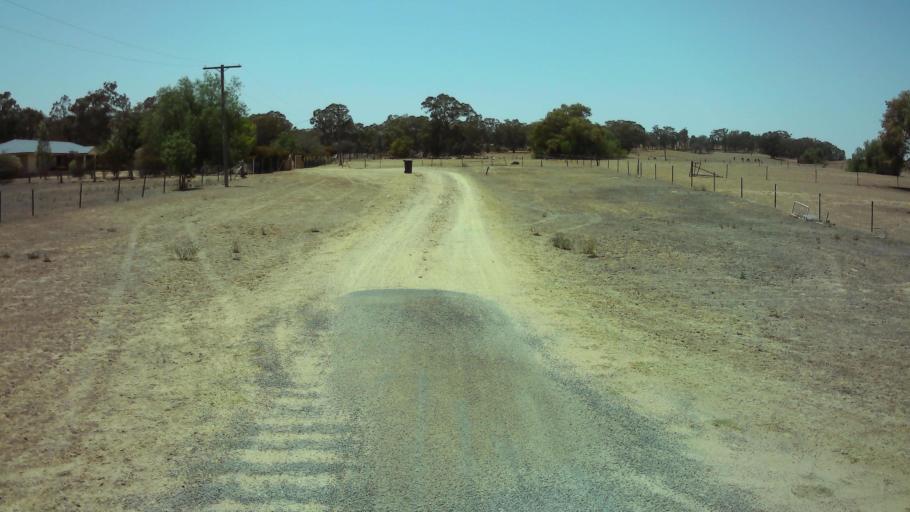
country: AU
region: New South Wales
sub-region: Weddin
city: Grenfell
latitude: -33.8919
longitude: 148.1724
